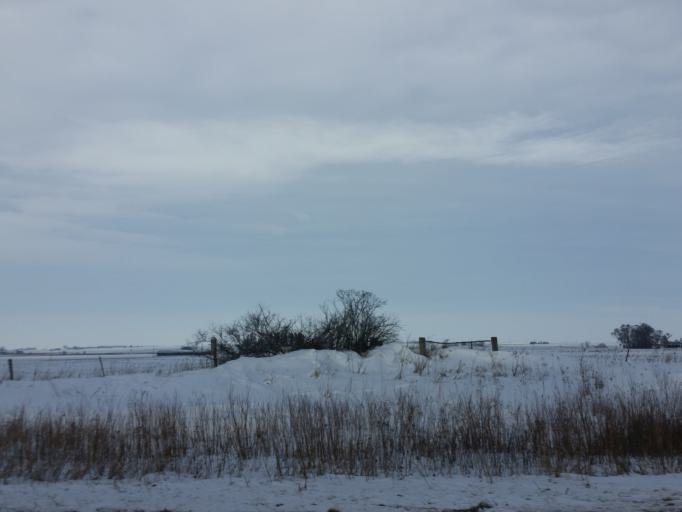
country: US
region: Iowa
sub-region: Delaware County
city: Manchester
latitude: 42.4646
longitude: -91.6267
